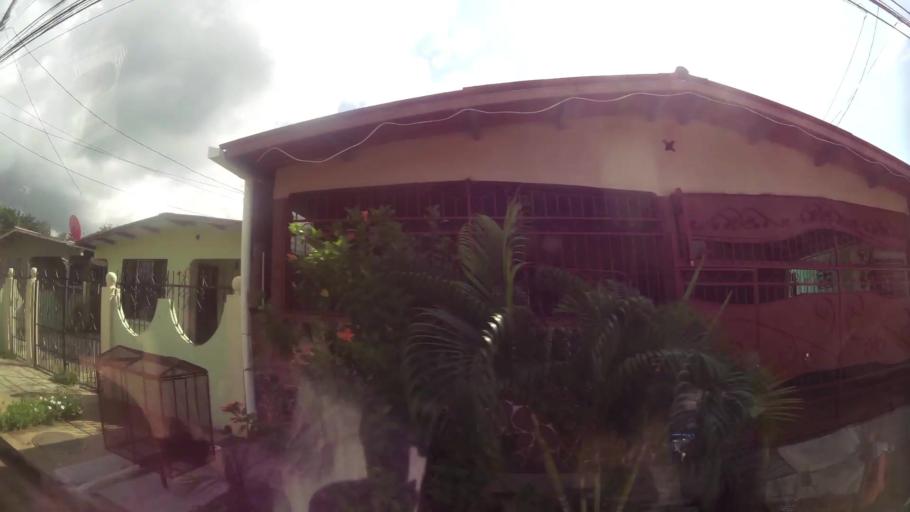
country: PA
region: Panama
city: Nuevo Arraijan
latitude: 8.9143
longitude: -79.7399
